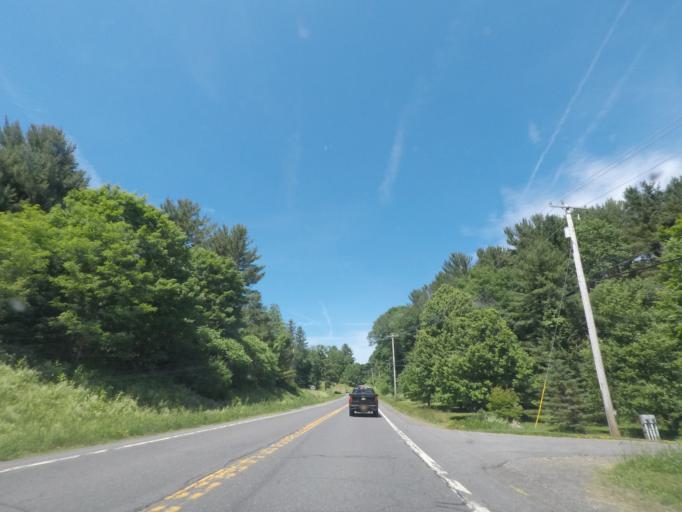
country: US
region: Massachusetts
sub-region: Berkshire County
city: Great Barrington
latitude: 42.1935
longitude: -73.5118
